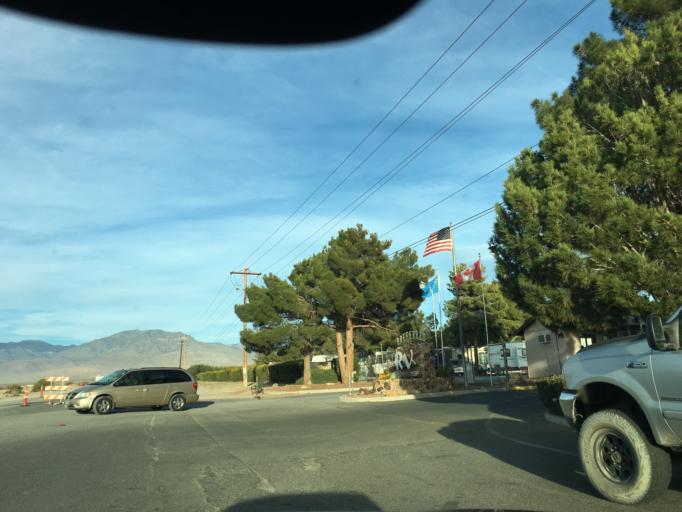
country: US
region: Nevada
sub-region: Nye County
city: Pahrump
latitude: 36.2111
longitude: -115.9823
